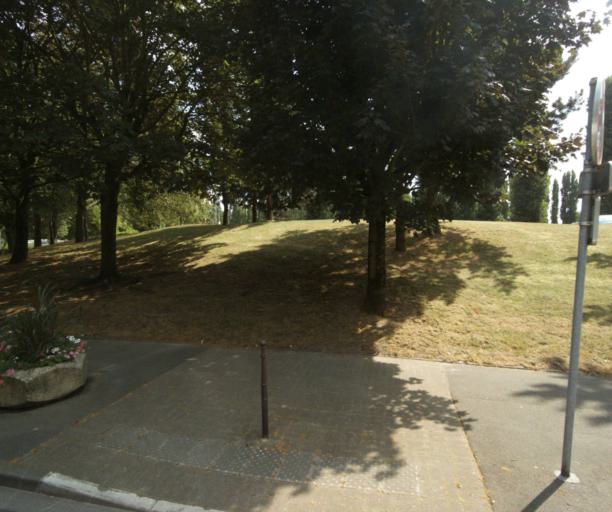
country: FR
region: Nord-Pas-de-Calais
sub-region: Departement du Nord
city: La Madeleine
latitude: 50.6510
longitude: 3.0672
